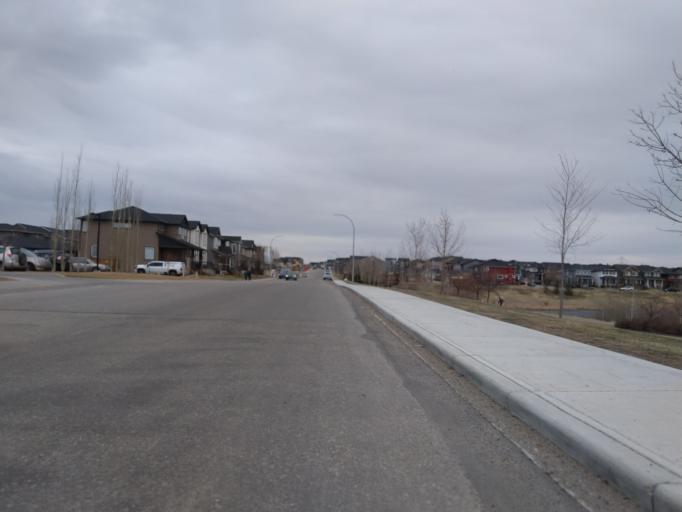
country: CA
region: Alberta
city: Calgary
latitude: 51.1739
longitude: -114.1051
